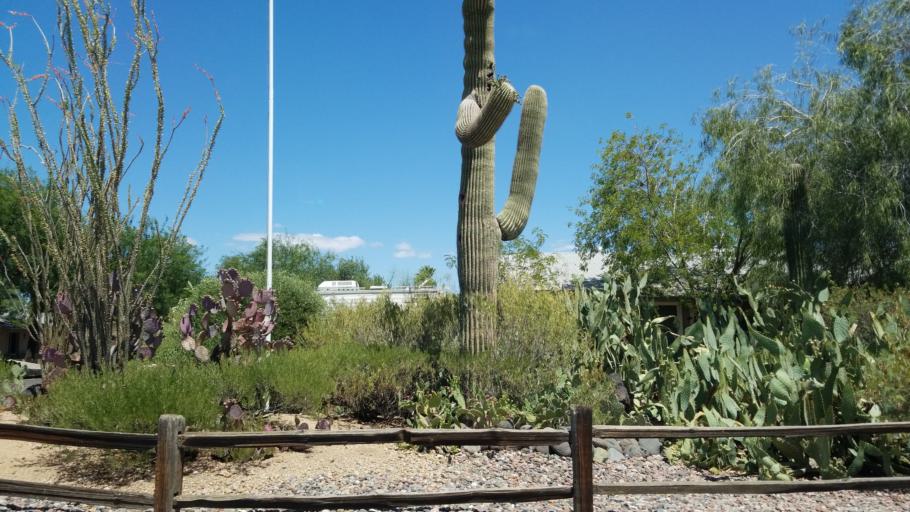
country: US
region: Arizona
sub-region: Maricopa County
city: Paradise Valley
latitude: 33.6070
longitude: -112.0210
